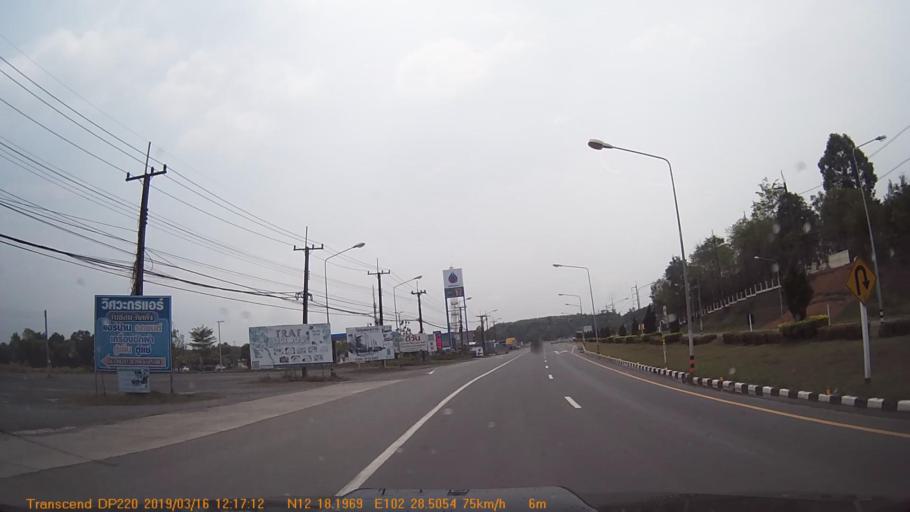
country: TH
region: Trat
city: Khao Saming
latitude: 12.3031
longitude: 102.4752
